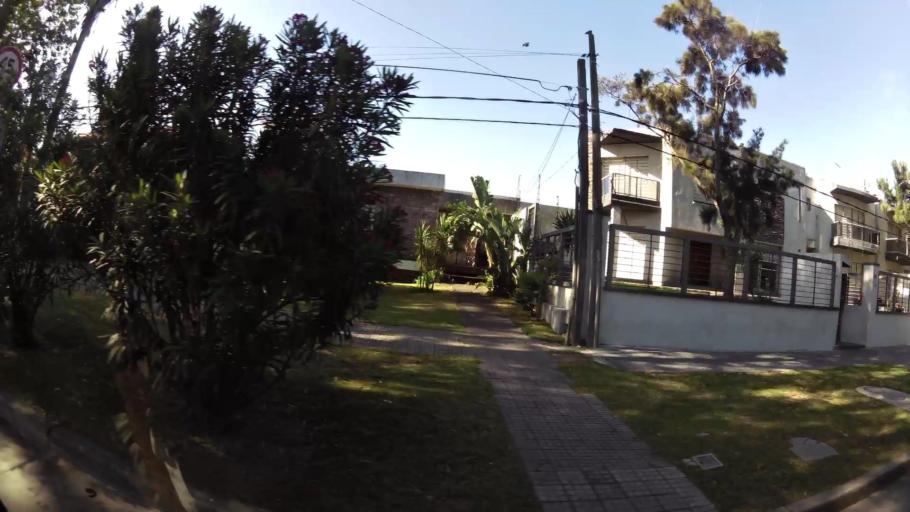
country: UY
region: Canelones
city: Paso de Carrasco
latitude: -34.8907
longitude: -56.0807
